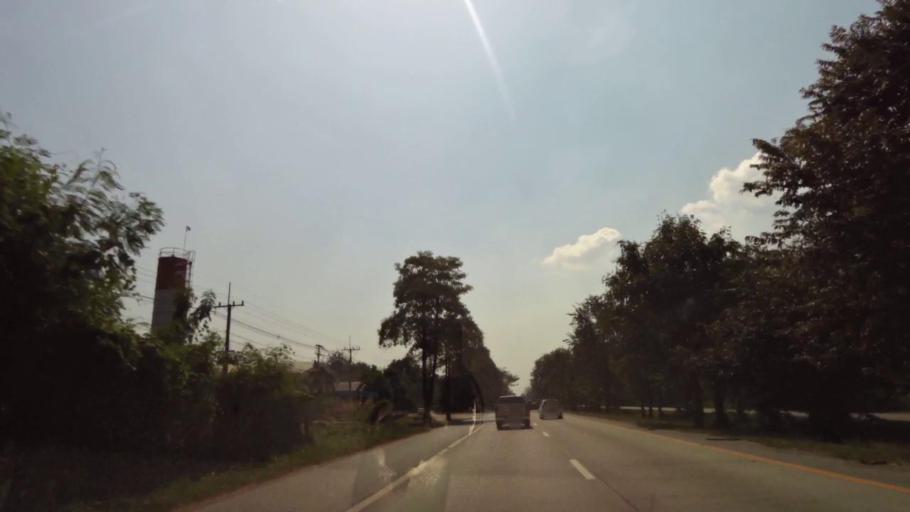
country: TH
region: Phichit
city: Wachira Barami
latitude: 16.5582
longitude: 100.1479
